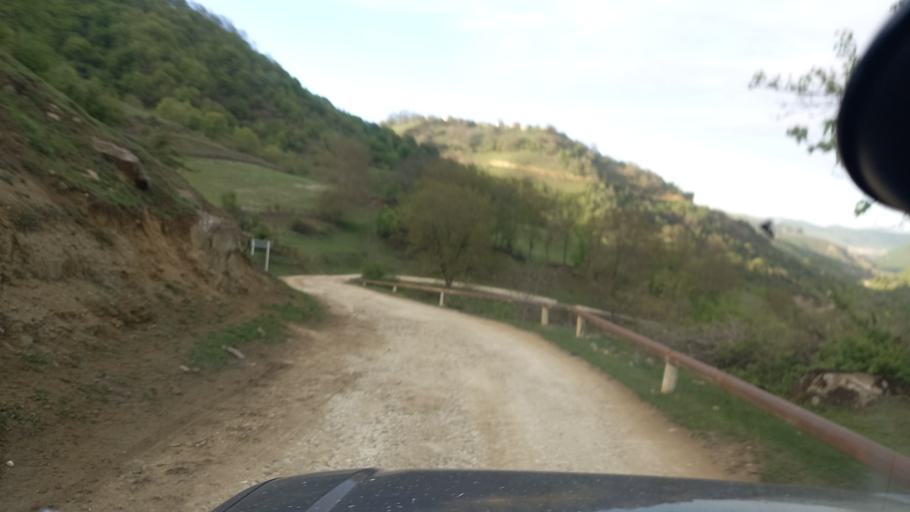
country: RU
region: Dagestan
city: Khuchni
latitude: 41.9480
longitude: 47.8357
